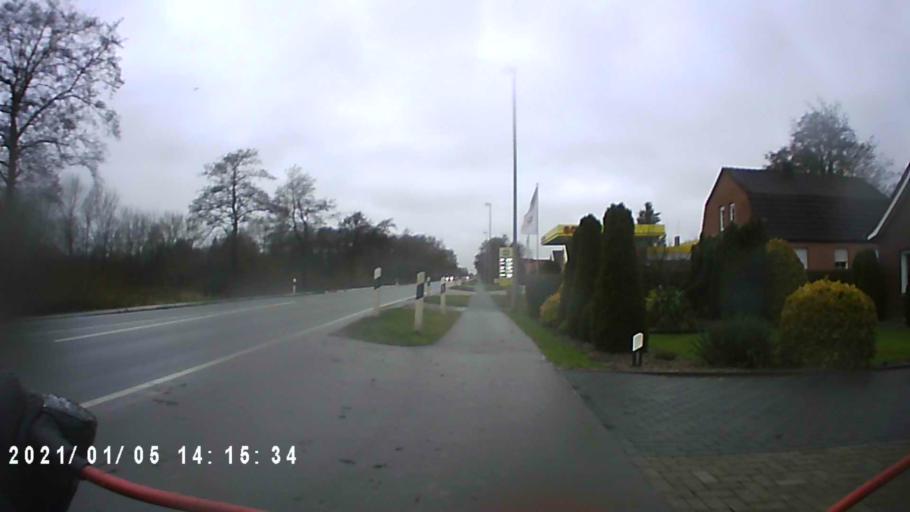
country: DE
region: Lower Saxony
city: Weener
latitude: 53.1743
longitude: 7.3127
